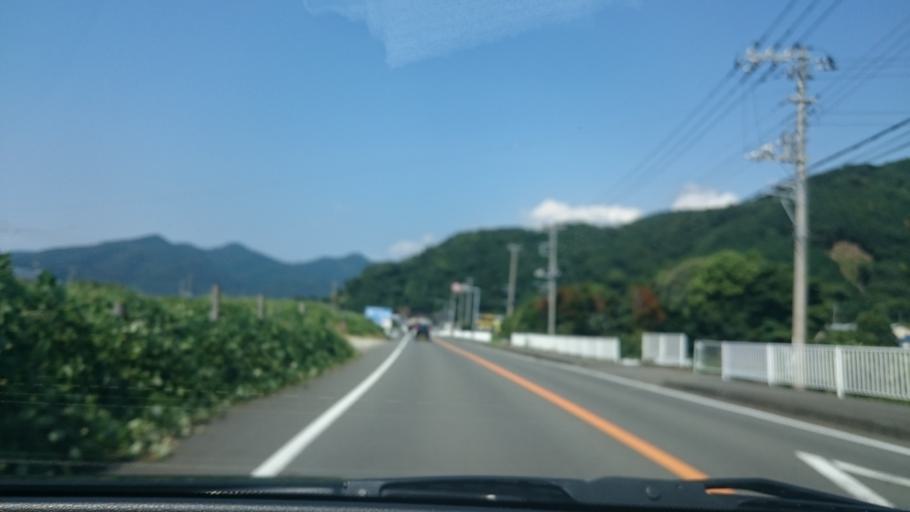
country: JP
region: Shizuoka
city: Heda
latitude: 34.8924
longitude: 138.7749
